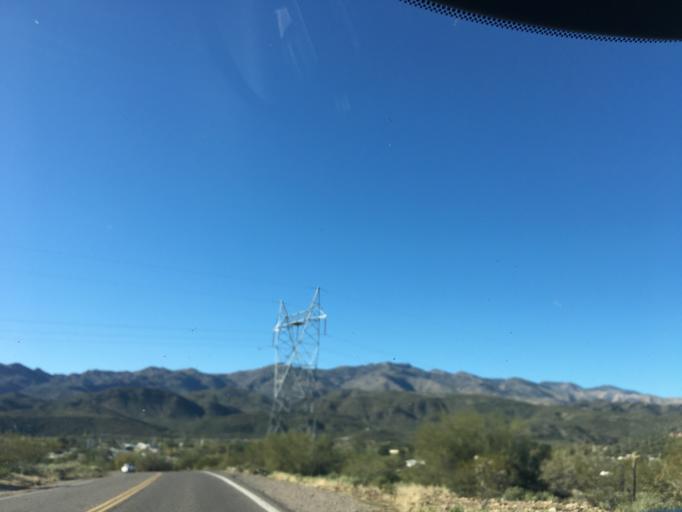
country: US
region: Arizona
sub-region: Yavapai County
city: Black Canyon City
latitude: 34.0658
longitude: -112.1438
